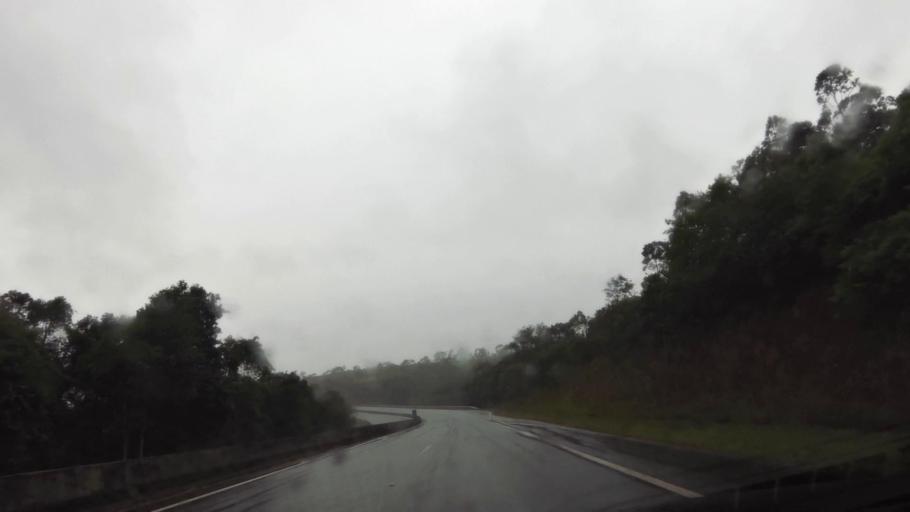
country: BR
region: Espirito Santo
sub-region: Guarapari
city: Guarapari
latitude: -20.6270
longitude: -40.5045
